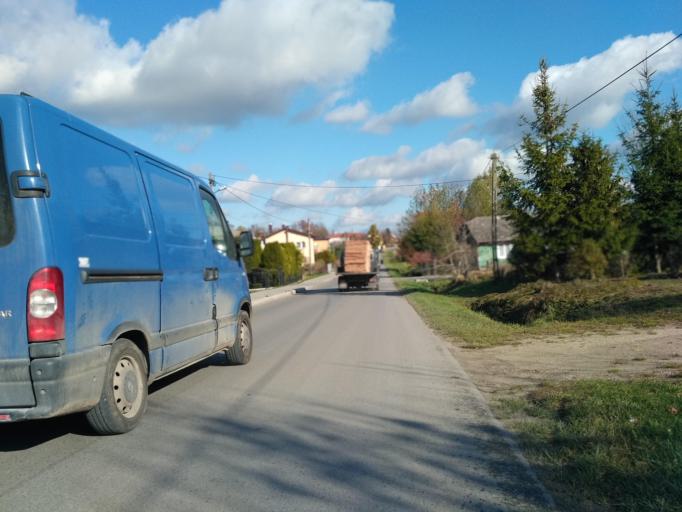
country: PL
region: Subcarpathian Voivodeship
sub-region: Powiat rzeszowski
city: Glogow Malopolski
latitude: 50.1369
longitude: 21.9060
